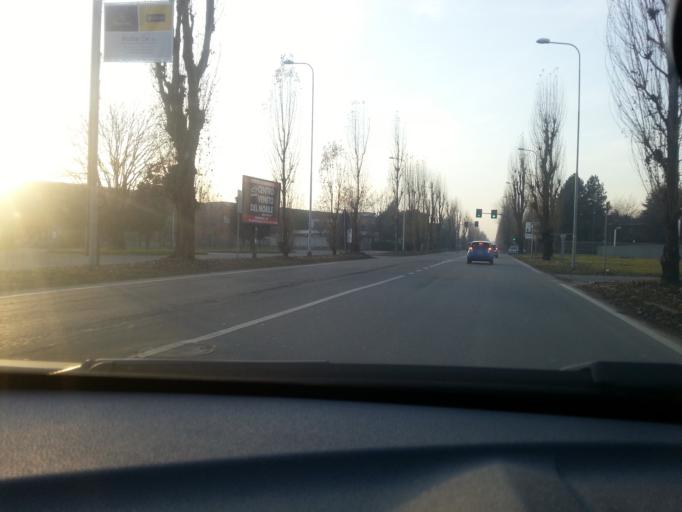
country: IT
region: Lombardy
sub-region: Citta metropolitana di Milano
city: Pero
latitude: 45.5287
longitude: 9.0799
